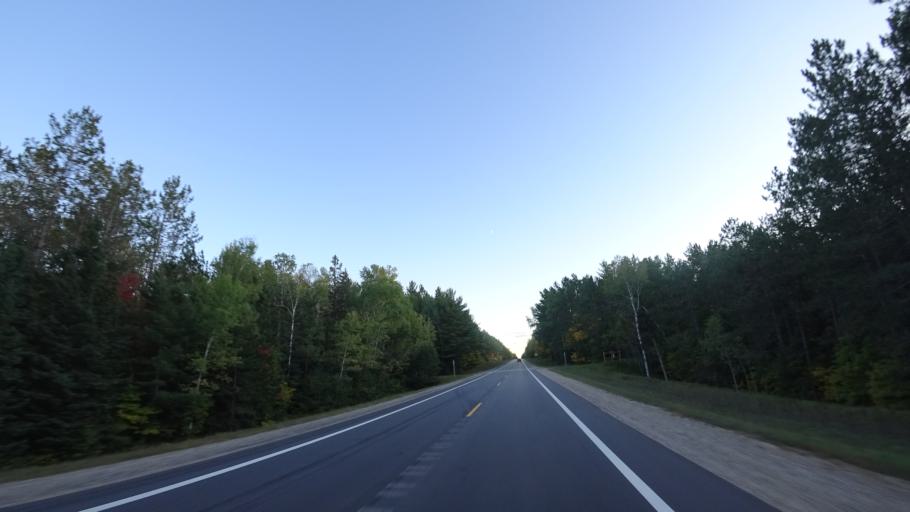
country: US
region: Michigan
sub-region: Luce County
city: Newberry
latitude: 46.3171
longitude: -85.0093
